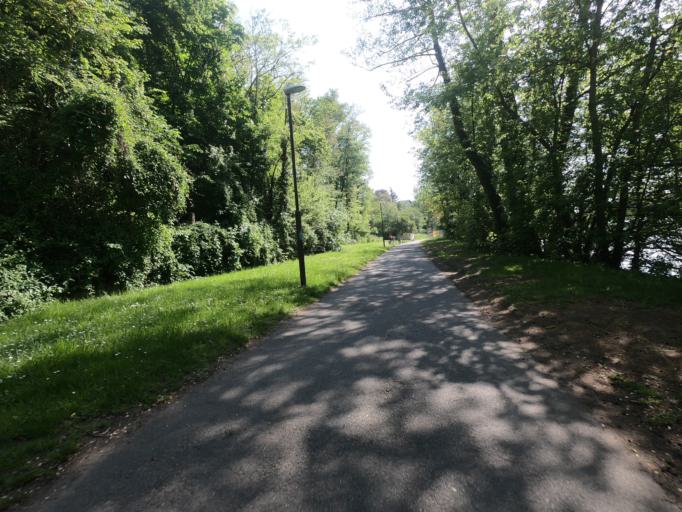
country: DE
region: Hesse
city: Kelsterbach
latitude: 50.0642
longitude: 8.5267
